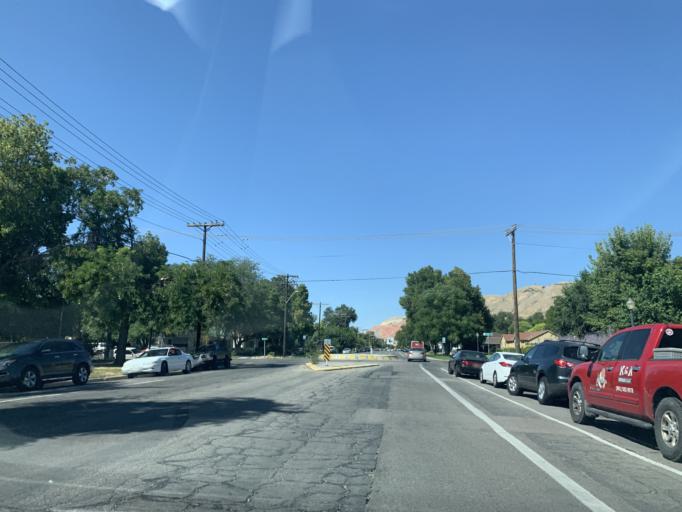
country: US
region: Utah
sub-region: Salt Lake County
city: Salt Lake City
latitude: 40.7732
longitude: -111.9082
